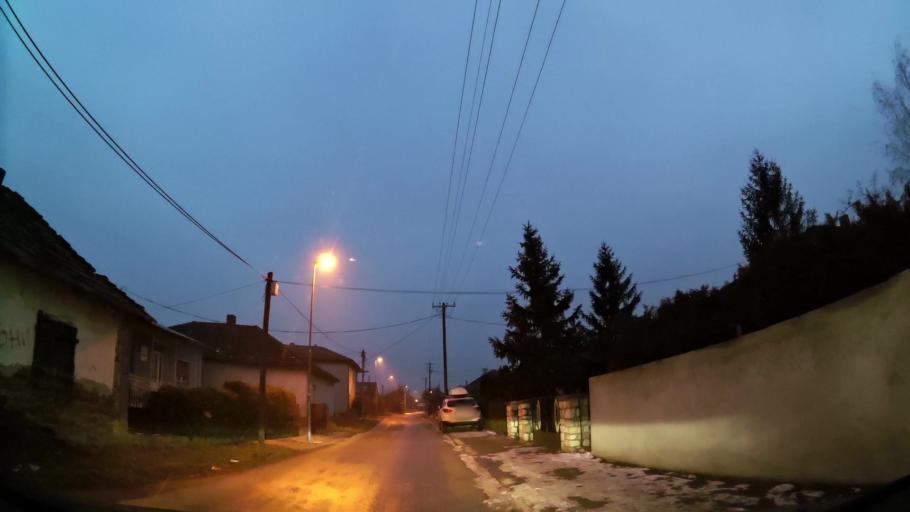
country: MK
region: Kisela Voda
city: Kisela Voda
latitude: 41.9672
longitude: 21.4853
